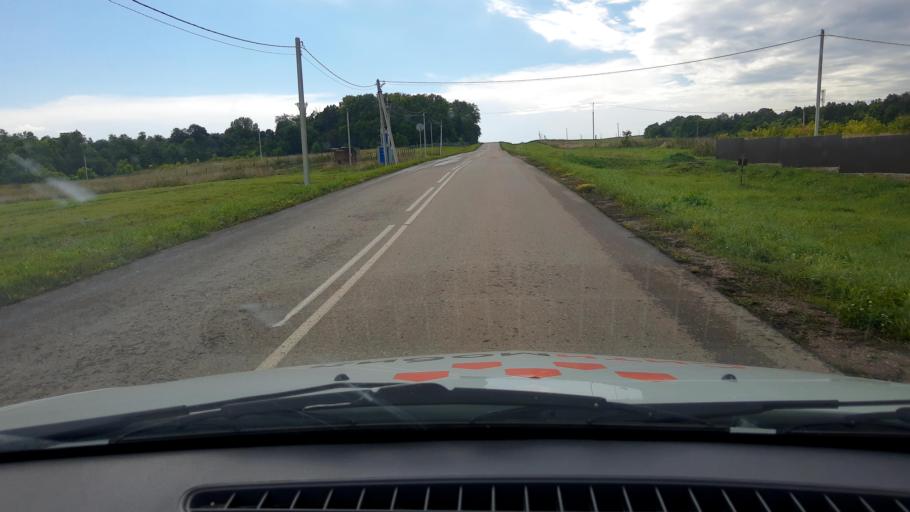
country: RU
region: Bashkortostan
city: Iglino
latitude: 54.9035
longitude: 56.1935
